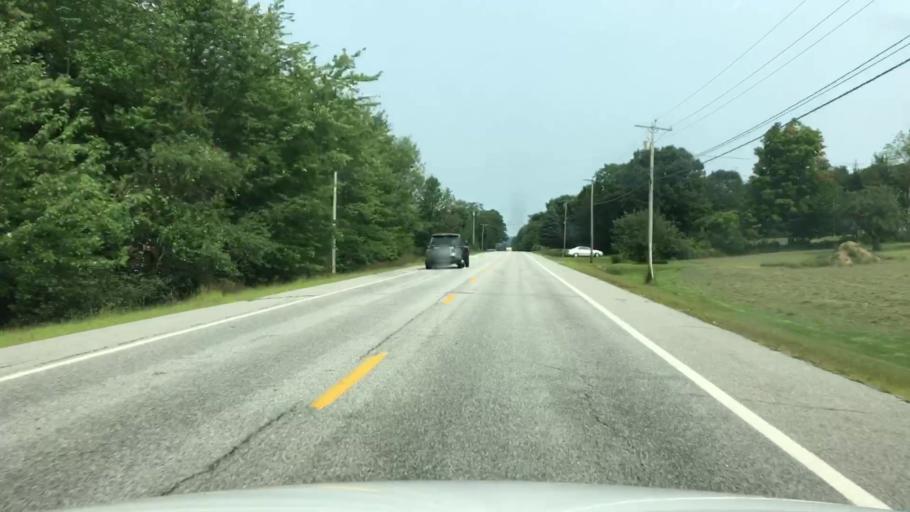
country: US
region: Maine
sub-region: Androscoggin County
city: Livermore Falls
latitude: 44.4352
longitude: -70.1473
